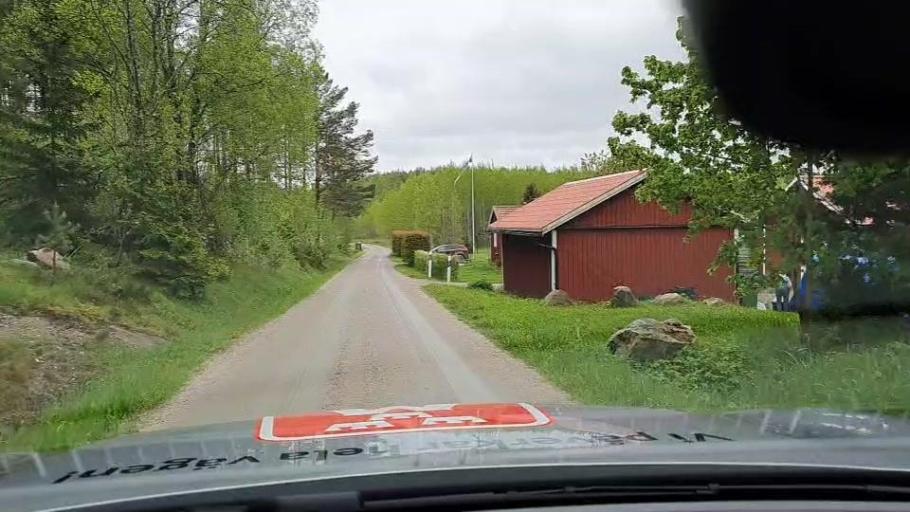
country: SE
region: Soedermanland
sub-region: Nykopings Kommun
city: Svalsta
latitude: 58.6239
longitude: 16.9386
